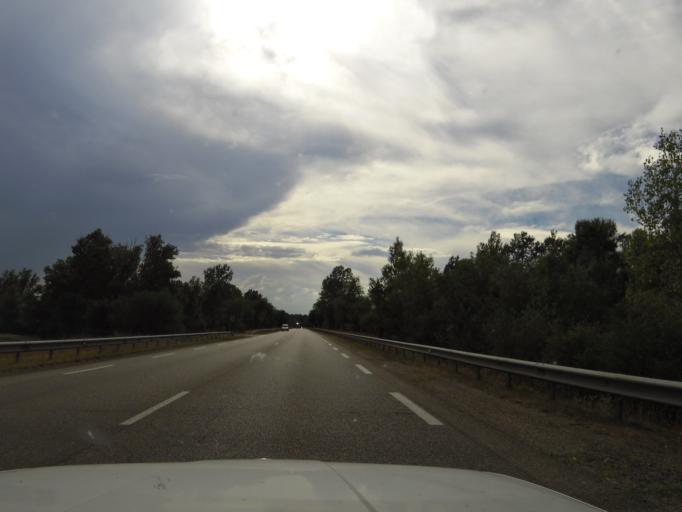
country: FR
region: Rhone-Alpes
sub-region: Departement de l'Ain
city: Saint-Jean-de-Niost
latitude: 45.8572
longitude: 5.2351
